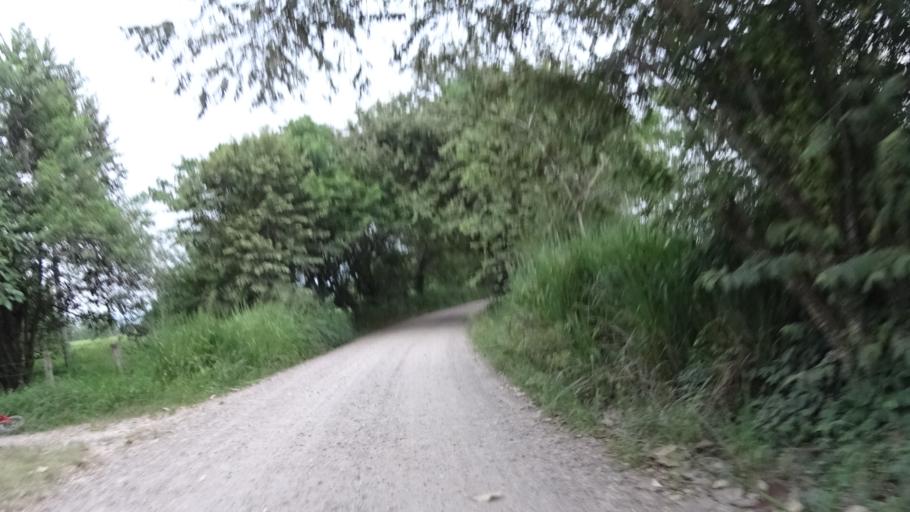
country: CO
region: Cundinamarca
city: Puerto Salgar
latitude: 5.4867
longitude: -74.6925
